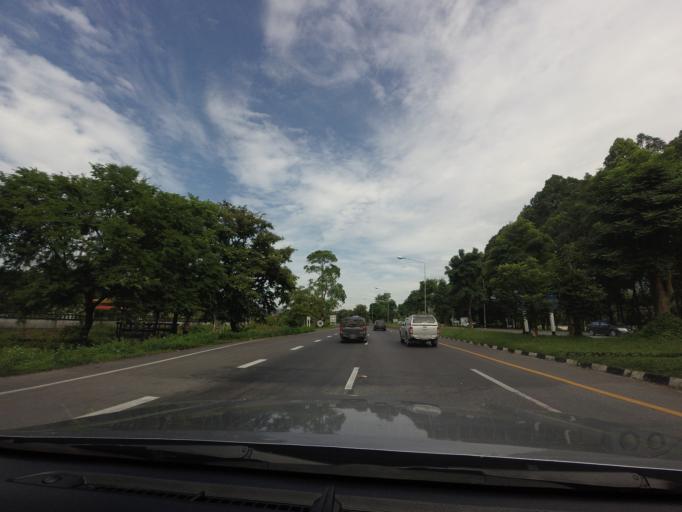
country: TH
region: Nakhon Si Thammarat
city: Ron Phibun
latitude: 8.1476
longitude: 99.8219
